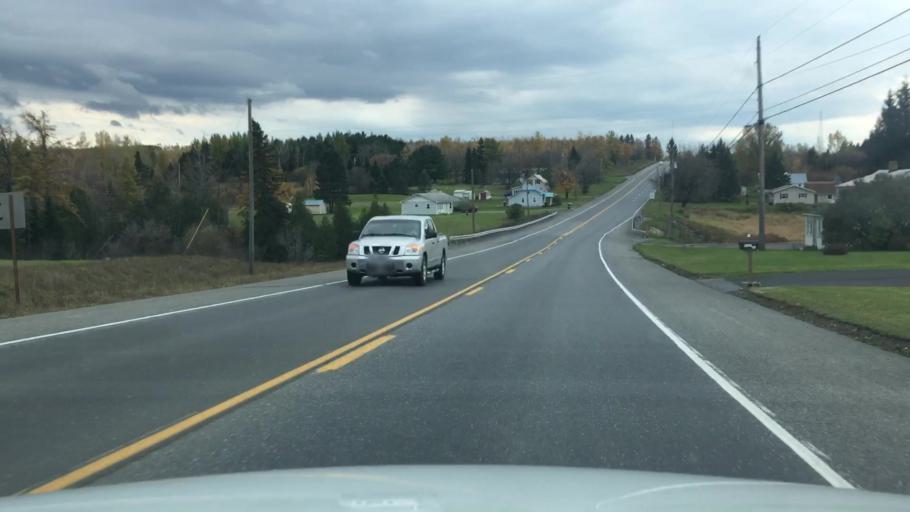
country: US
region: Maine
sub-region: Aroostook County
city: Caribou
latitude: 46.7847
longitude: -67.9891
